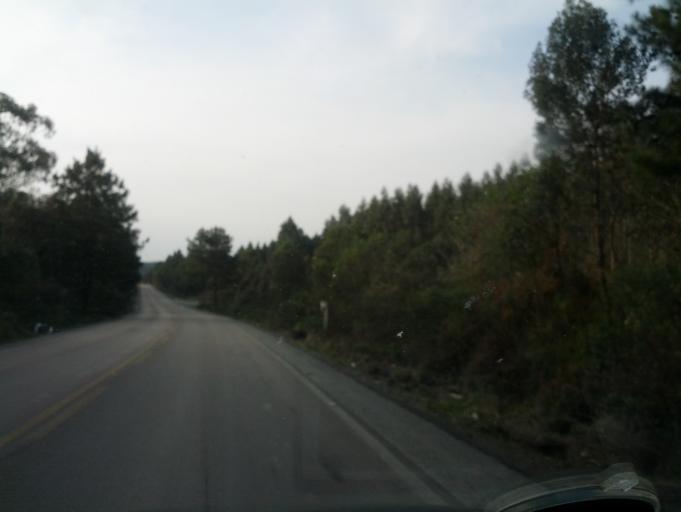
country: BR
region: Santa Catarina
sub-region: Otacilio Costa
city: Otacilio Costa
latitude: -27.4267
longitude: -50.1214
